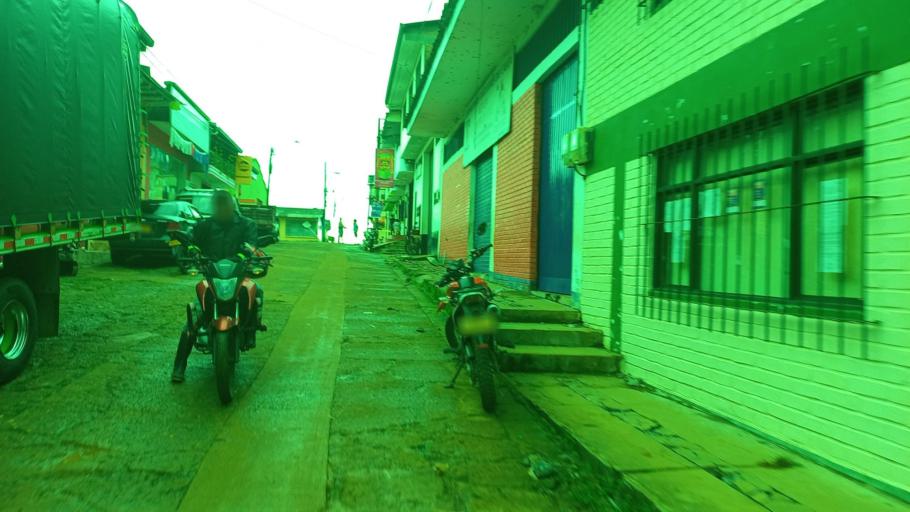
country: CO
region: Cauca
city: Balboa
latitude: 2.0405
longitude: -77.2157
